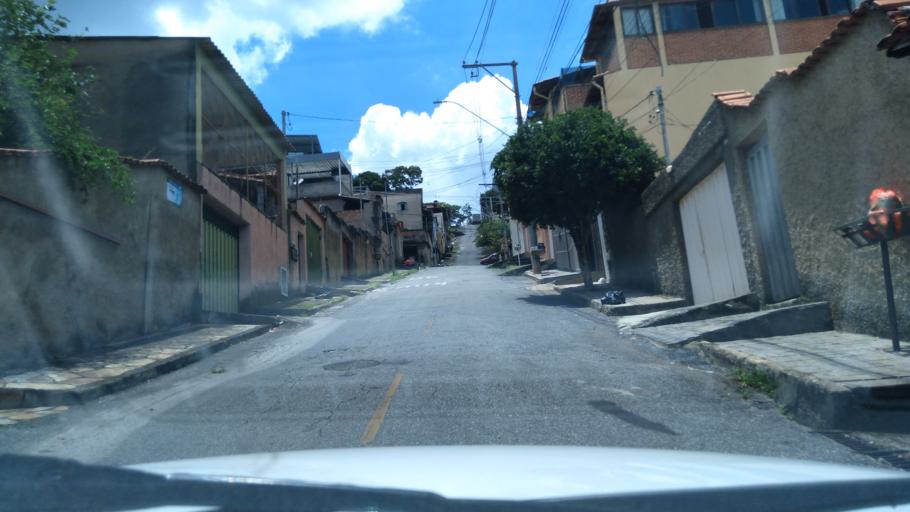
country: BR
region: Minas Gerais
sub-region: Belo Horizonte
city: Belo Horizonte
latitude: -19.9233
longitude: -43.9016
